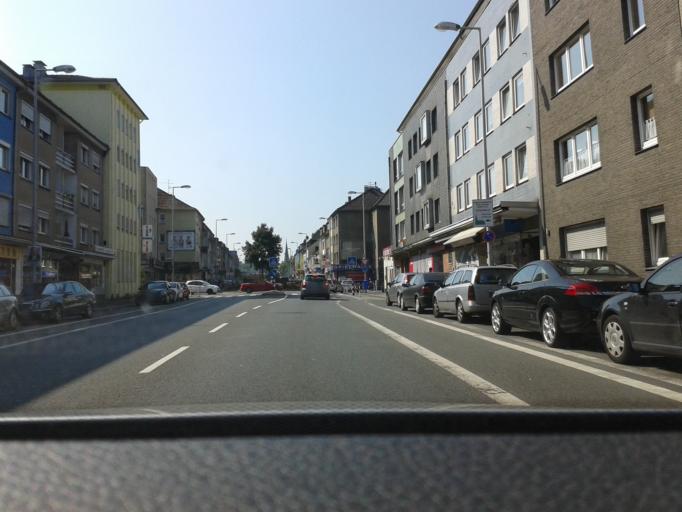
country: DE
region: North Rhine-Westphalia
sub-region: Regierungsbezirk Dusseldorf
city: Muelheim (Ruhr)
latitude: 51.4344
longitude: 6.8872
